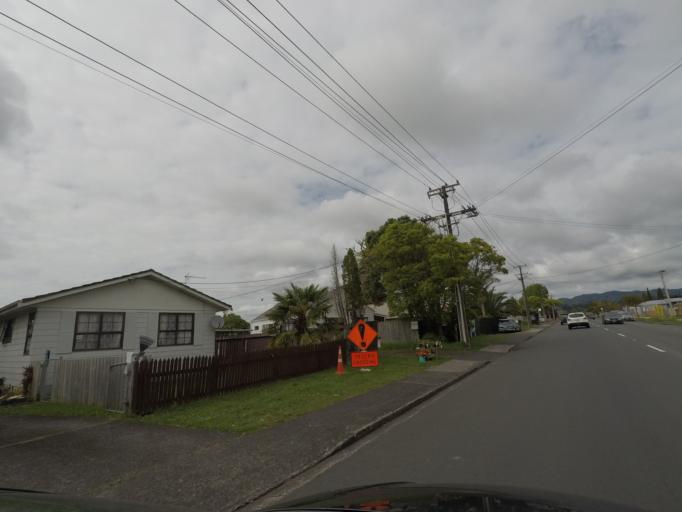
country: NZ
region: Auckland
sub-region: Auckland
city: Waitakere
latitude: -36.8977
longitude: 174.6253
